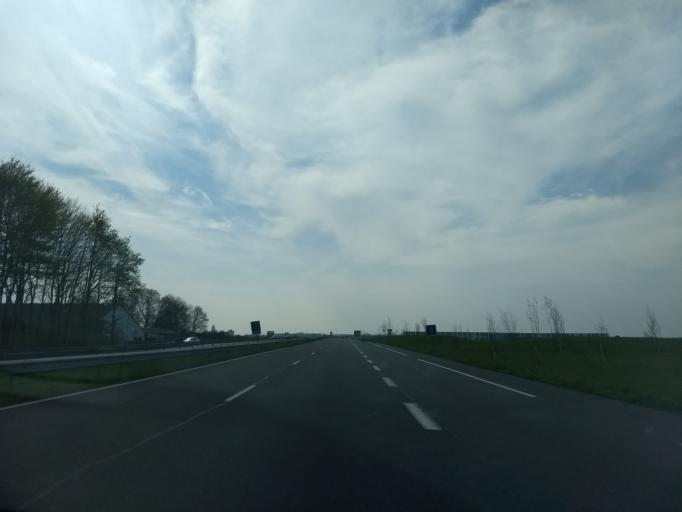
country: FR
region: Nord-Pas-de-Calais
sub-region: Departement du Nord
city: Courchelettes
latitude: 50.3548
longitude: 3.0441
